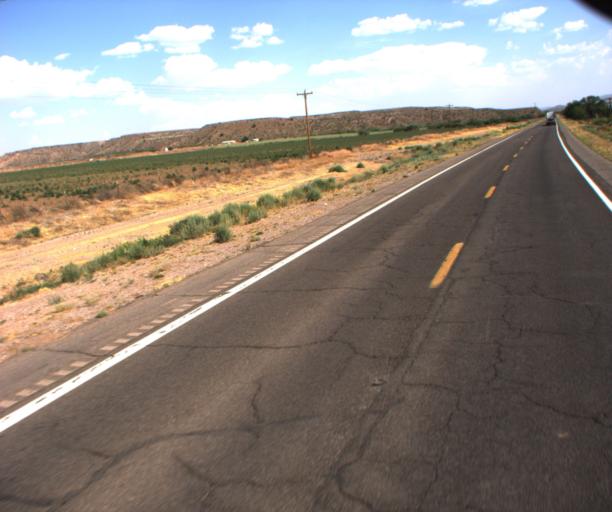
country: US
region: Arizona
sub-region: Greenlee County
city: Clifton
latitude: 32.8545
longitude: -109.1822
